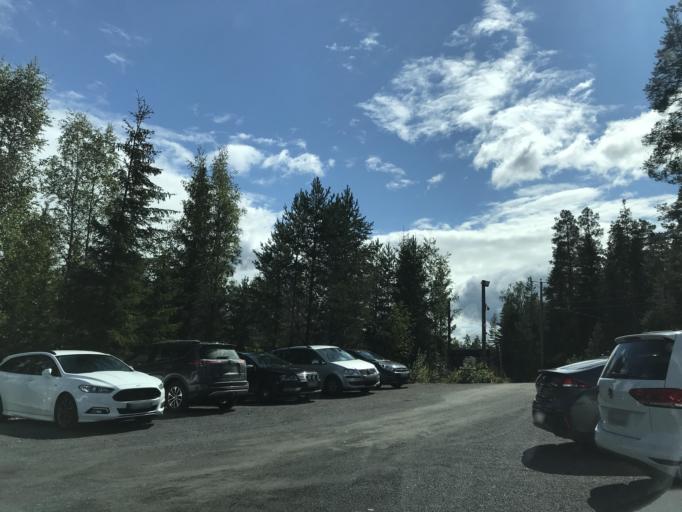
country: FI
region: Haeme
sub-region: Forssa
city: Tammela
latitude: 60.6304
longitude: 23.7552
